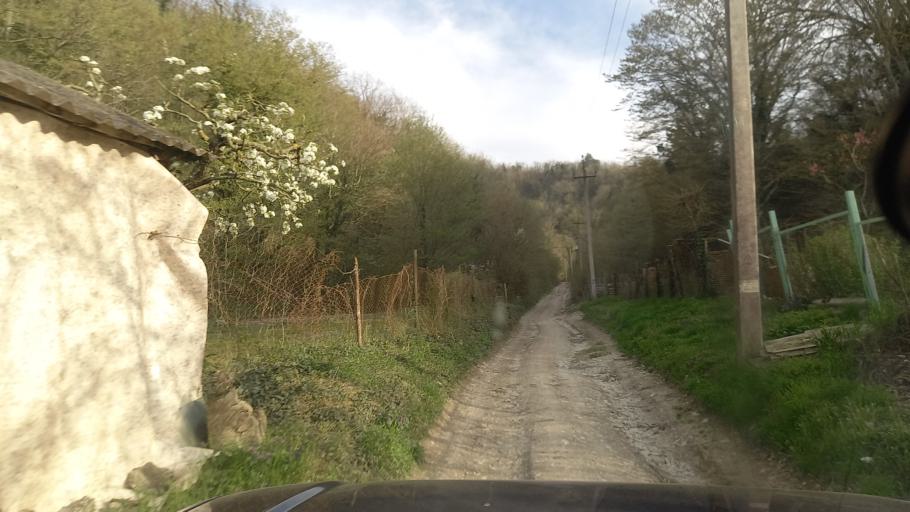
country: RU
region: Krasnodarskiy
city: Arkhipo-Osipovka
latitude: 44.3700
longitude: 38.5841
